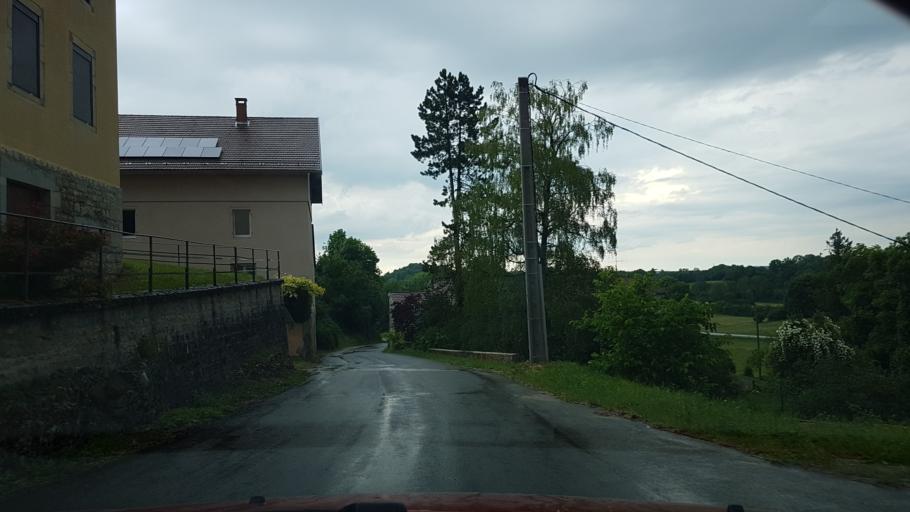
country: FR
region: Franche-Comte
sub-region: Departement du Jura
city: Clairvaux-les-Lacs
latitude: 46.5419
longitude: 5.7486
